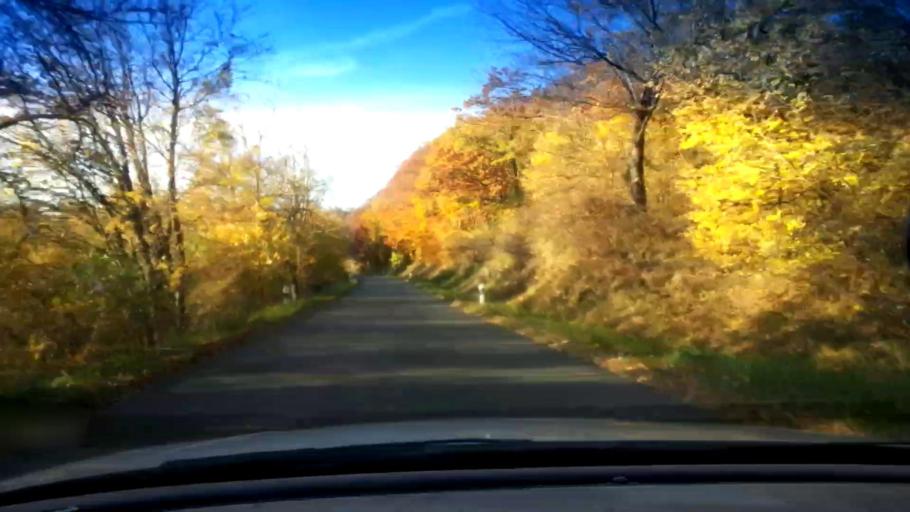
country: DE
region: Bavaria
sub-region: Upper Franconia
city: Heiligenstadt
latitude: 49.8655
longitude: 11.1803
